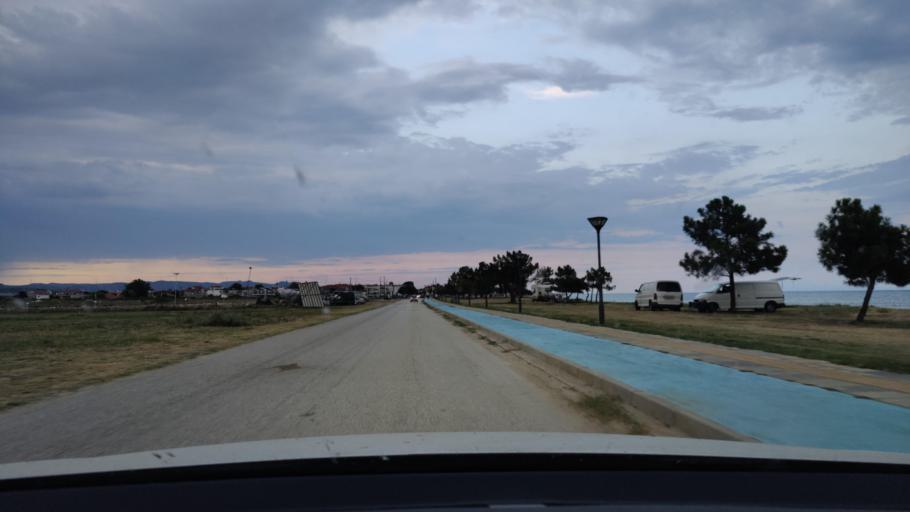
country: GR
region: East Macedonia and Thrace
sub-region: Nomos Kavalas
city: Paralia Ofryniou
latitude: 40.7685
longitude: 23.8934
